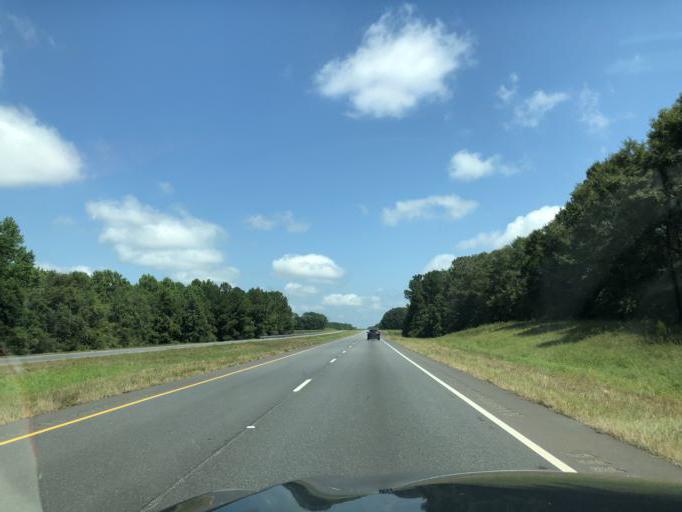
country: US
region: Alabama
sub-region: Henry County
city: Abbeville
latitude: 31.4805
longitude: -85.3002
